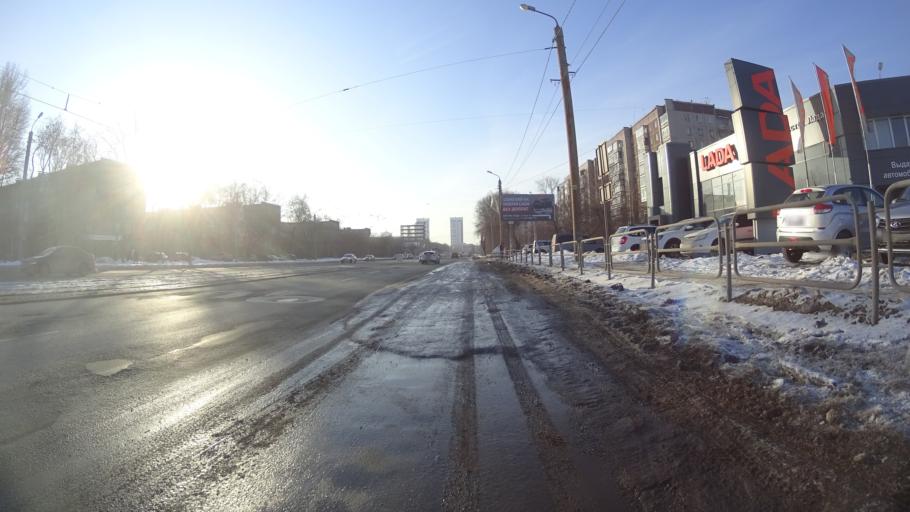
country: RU
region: Chelyabinsk
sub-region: Gorod Chelyabinsk
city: Chelyabinsk
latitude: 55.1683
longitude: 61.4270
